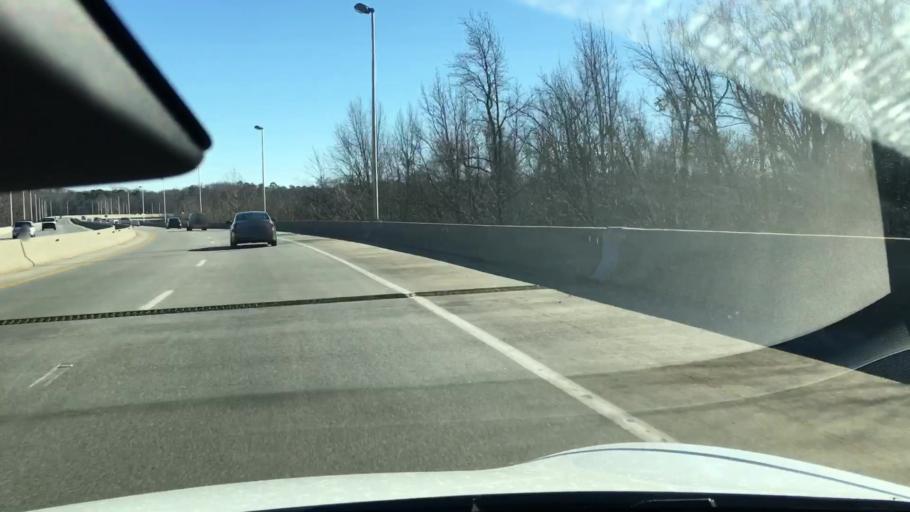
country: US
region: Virginia
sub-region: Henrico County
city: Tuckahoe
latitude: 37.5631
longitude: -77.5763
